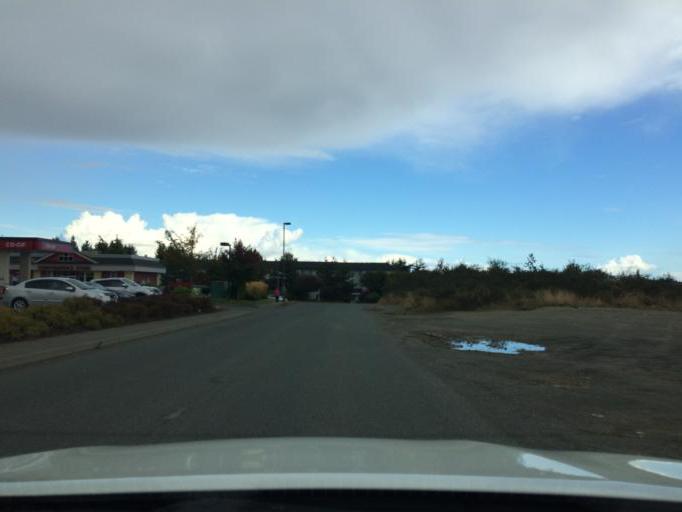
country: CA
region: British Columbia
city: Courtenay
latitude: 49.6879
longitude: -124.9448
